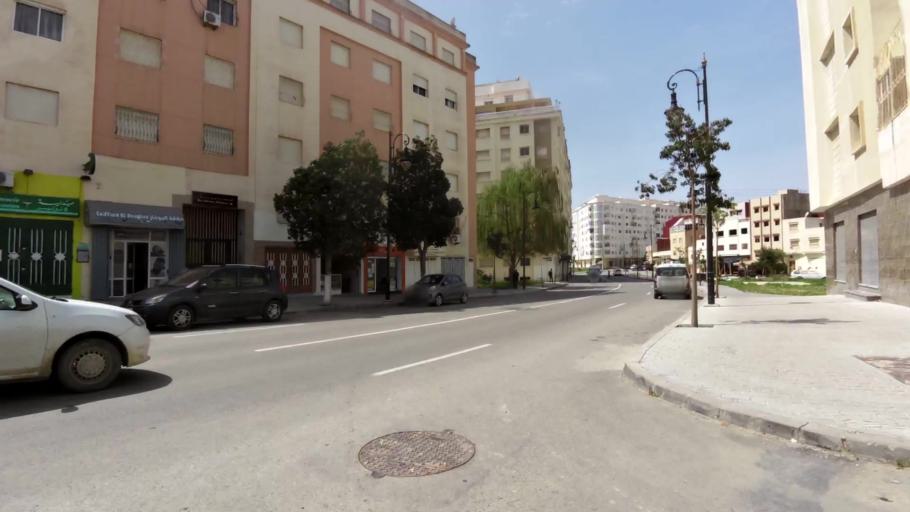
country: MA
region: Tanger-Tetouan
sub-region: Tanger-Assilah
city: Tangier
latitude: 35.7455
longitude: -5.8475
